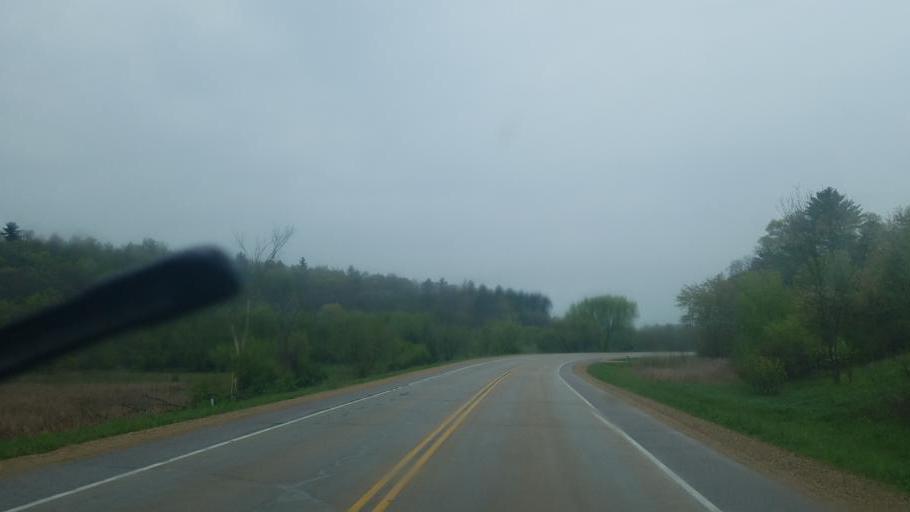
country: US
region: Wisconsin
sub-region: Juneau County
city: Elroy
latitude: 43.6409
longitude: -90.2049
